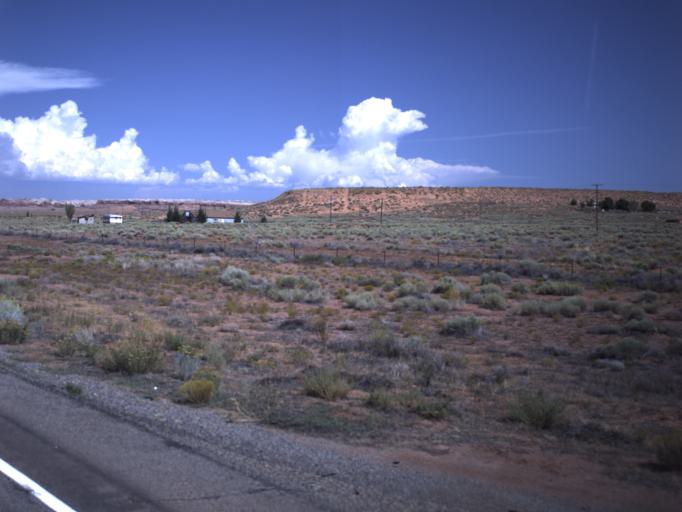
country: US
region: Utah
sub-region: San Juan County
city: Blanding
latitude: 37.1546
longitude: -109.5689
